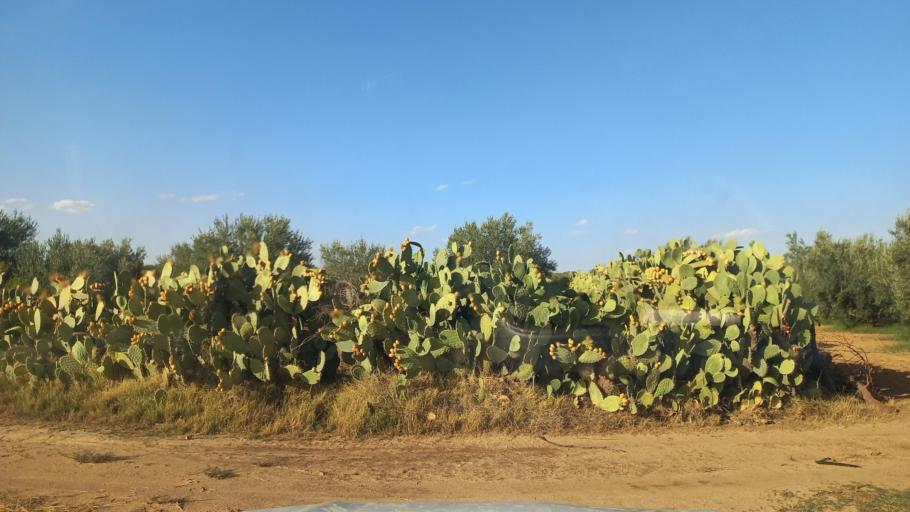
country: TN
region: Al Qasrayn
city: Kasserine
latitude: 35.2652
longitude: 9.0333
